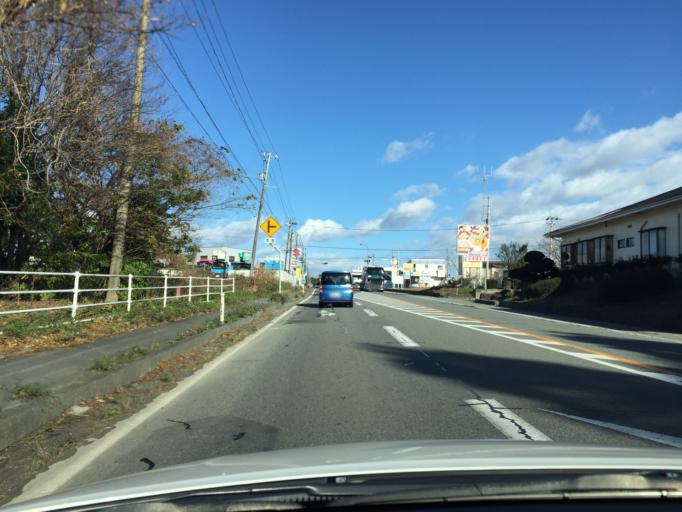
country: JP
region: Fukushima
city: Namie
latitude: 37.2954
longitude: 140.9941
